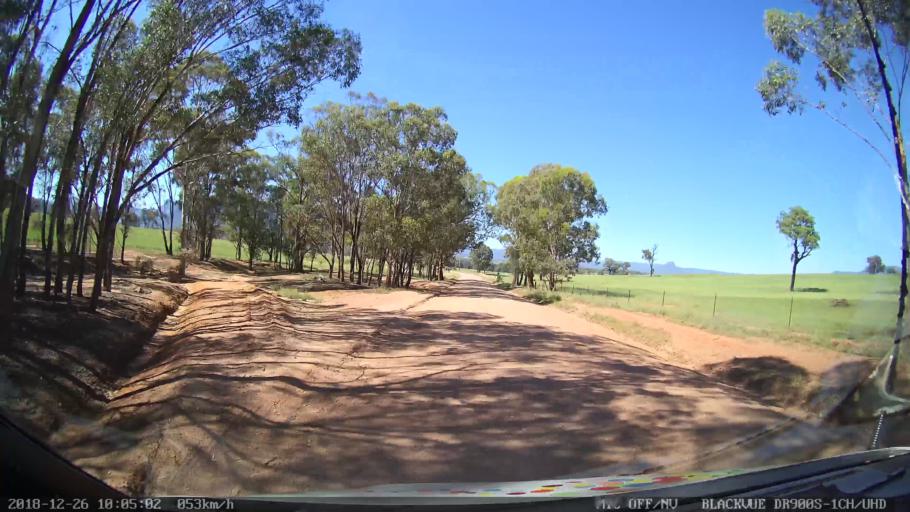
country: AU
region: New South Wales
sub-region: Mid-Western Regional
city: Kandos
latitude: -33.0752
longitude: 150.2123
